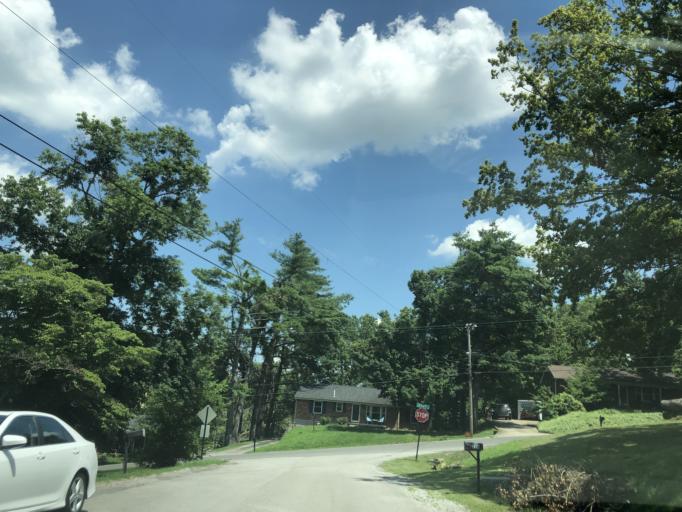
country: US
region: Tennessee
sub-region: Davidson County
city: Lakewood
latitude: 36.1770
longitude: -86.6493
